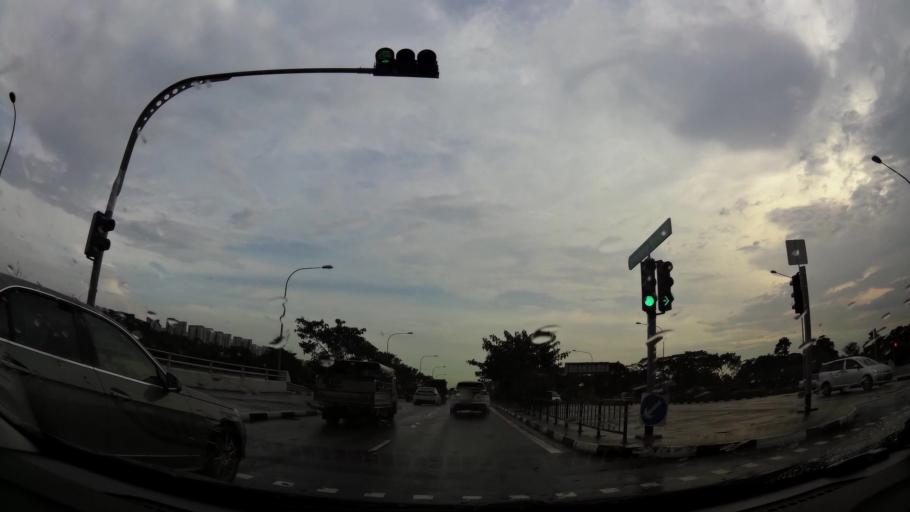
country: MY
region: Johor
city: Kampung Pasir Gudang Baru
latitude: 1.4005
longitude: 103.8690
